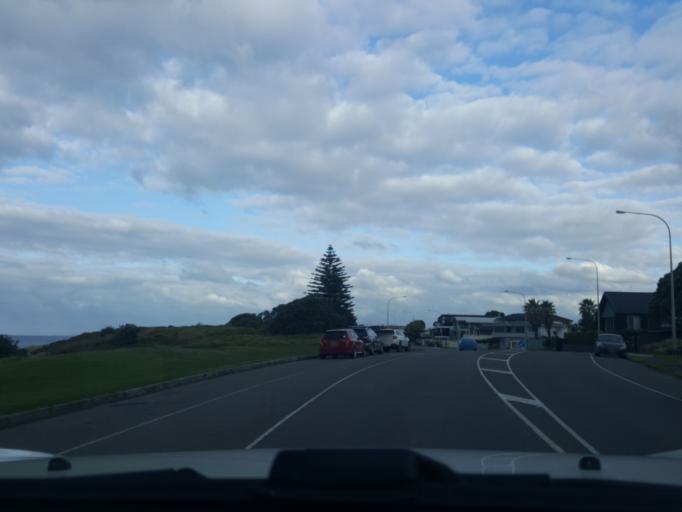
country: NZ
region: Bay of Plenty
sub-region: Tauranga City
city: Tauranga
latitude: -37.6510
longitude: 176.2039
